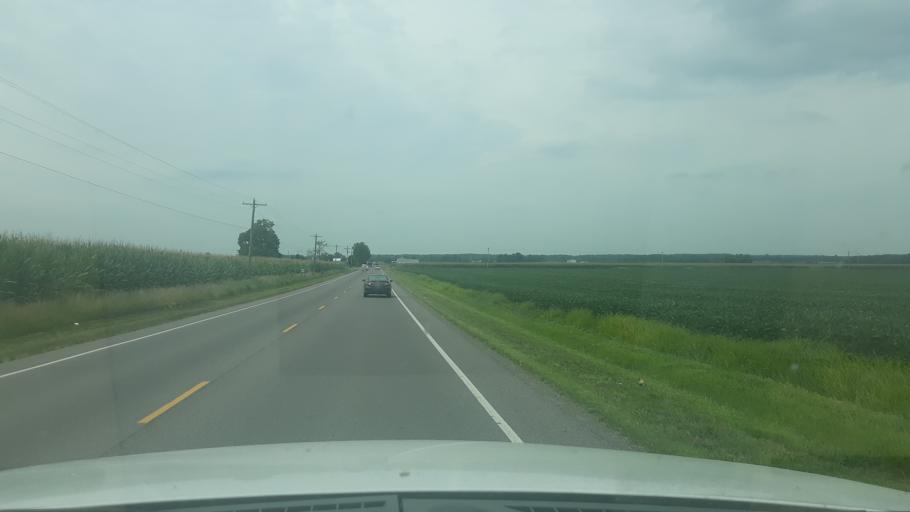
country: US
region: Illinois
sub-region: Saline County
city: Harrisburg
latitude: 37.8018
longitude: -88.5399
